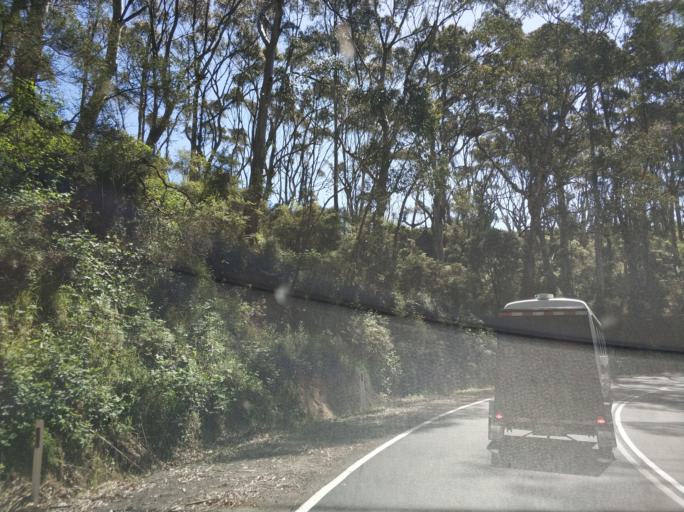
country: AU
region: Victoria
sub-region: Colac-Otway
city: Apollo Bay
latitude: -38.7422
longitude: 143.2528
